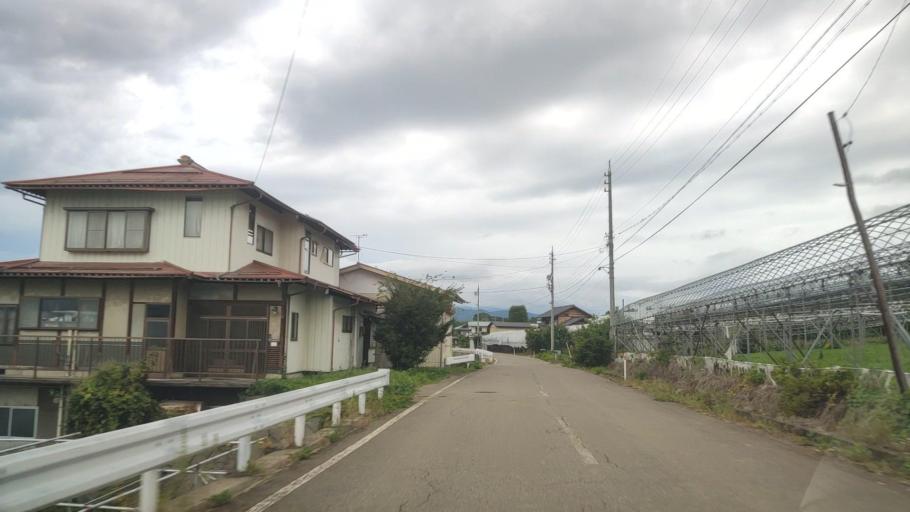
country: JP
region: Nagano
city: Nakano
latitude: 36.7788
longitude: 138.3752
